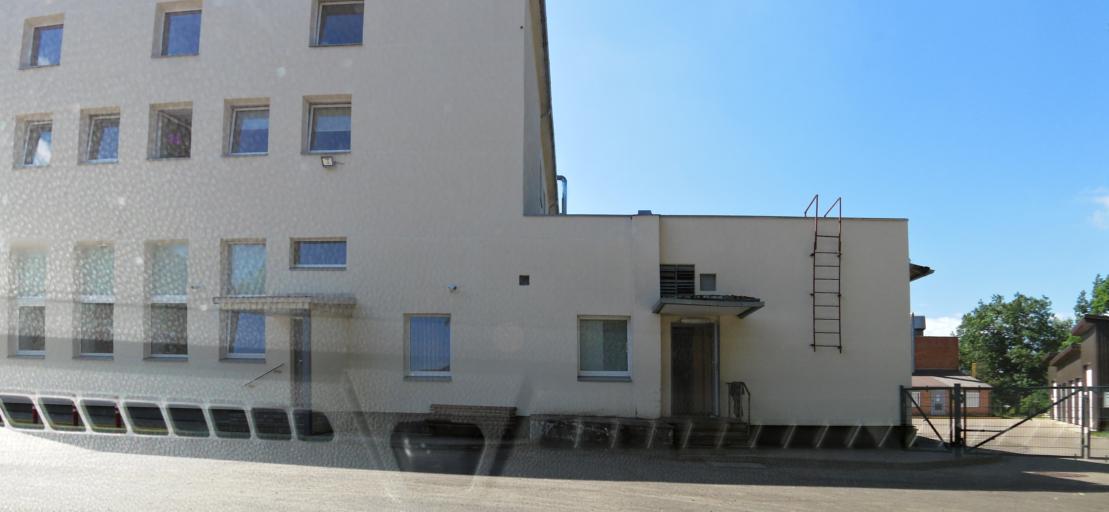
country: LT
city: Nemencine
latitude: 54.7940
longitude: 25.3968
